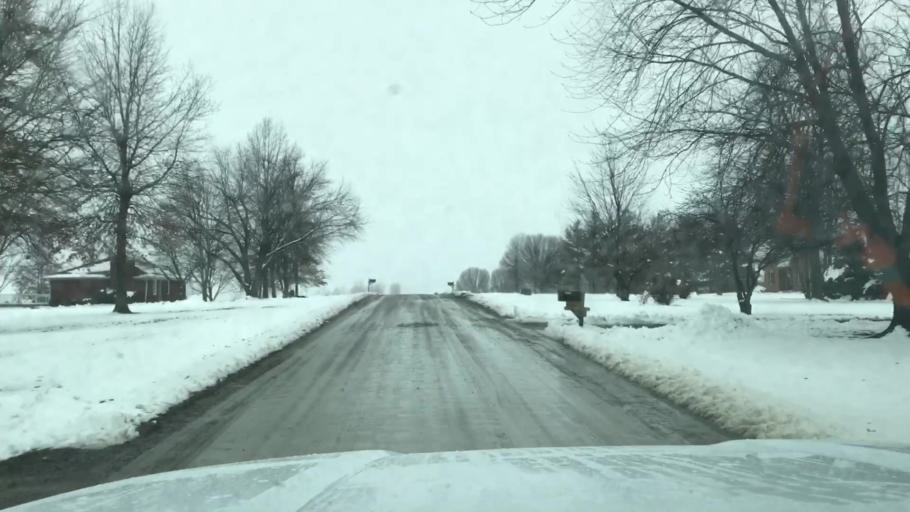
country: US
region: Missouri
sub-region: Clinton County
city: Cameron
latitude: 39.7296
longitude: -94.2128
